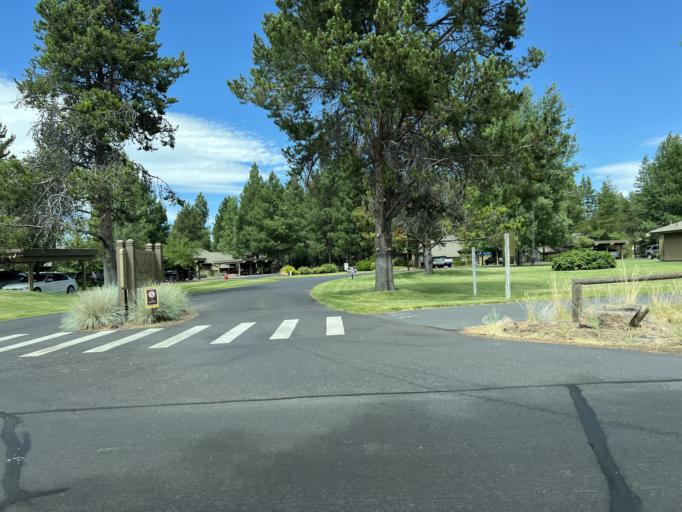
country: US
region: Oregon
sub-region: Deschutes County
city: Sunriver
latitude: 43.8831
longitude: -121.4431
